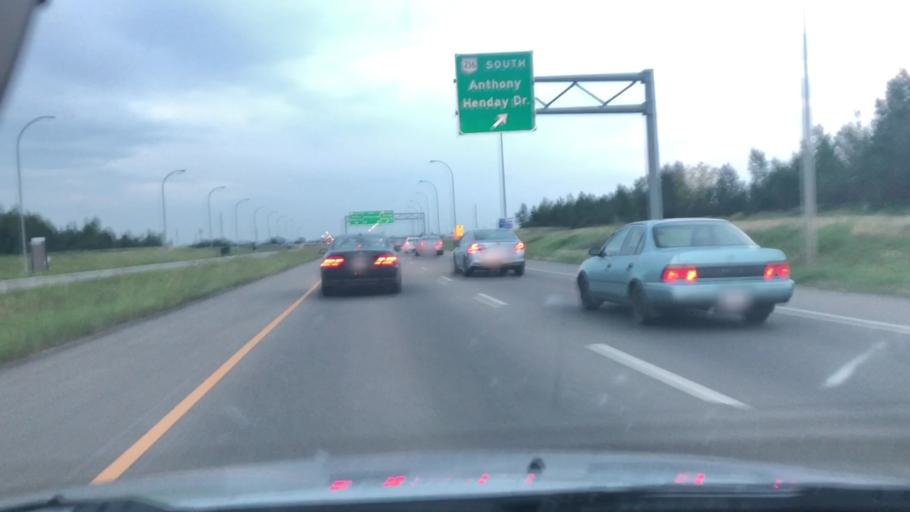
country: CA
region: Alberta
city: St. Albert
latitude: 53.5122
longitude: -113.6710
